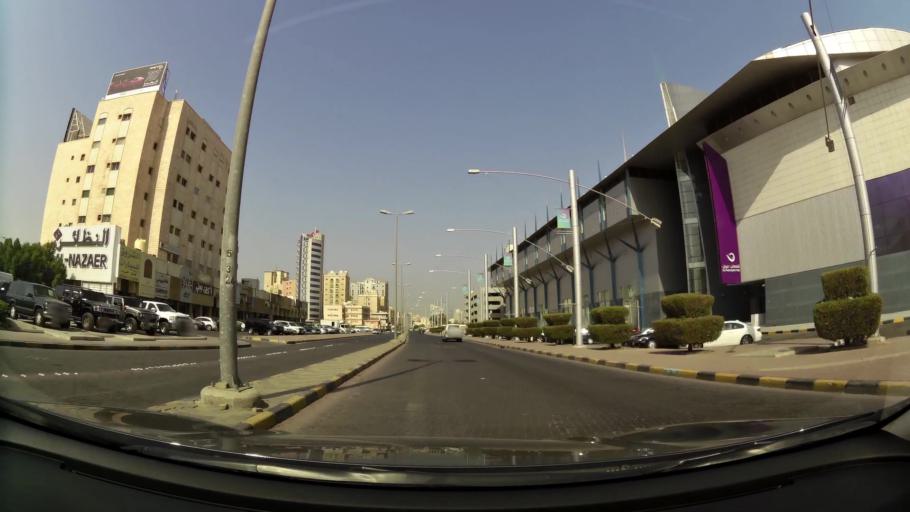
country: KW
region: Muhafazat Hawalli
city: Hawalli
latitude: 29.3400
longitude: 48.0262
